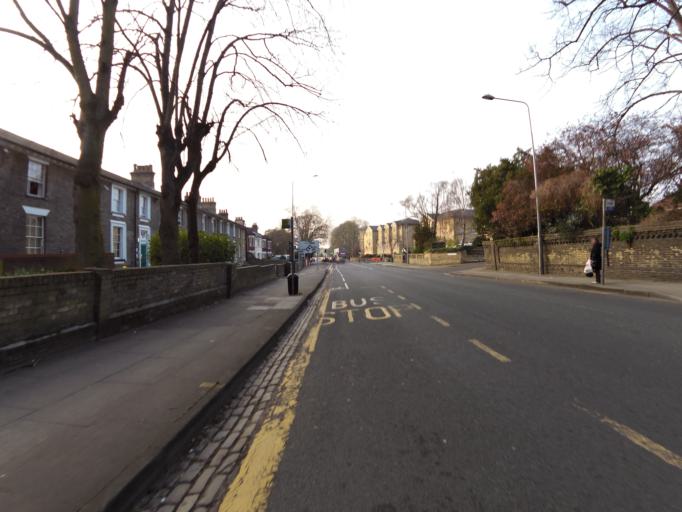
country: GB
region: England
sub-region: Suffolk
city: Ipswich
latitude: 52.0641
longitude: 1.1409
